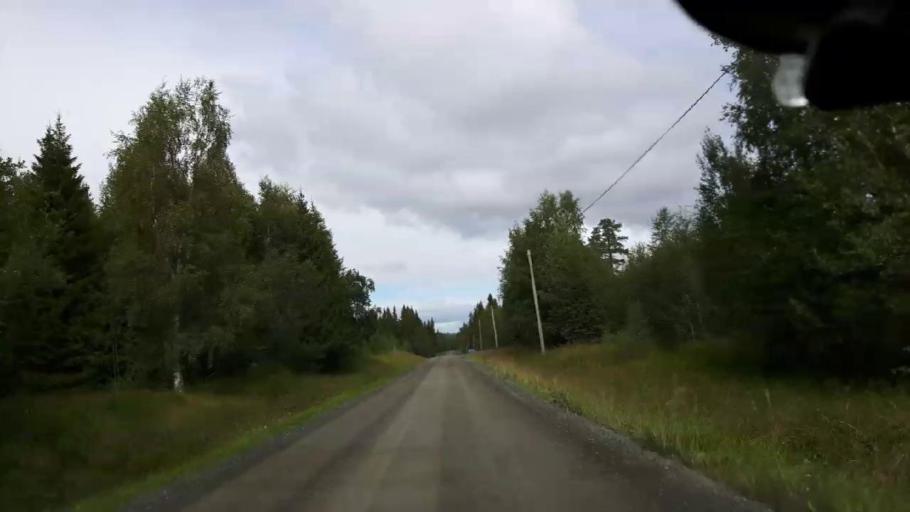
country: SE
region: Jaemtland
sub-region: Krokoms Kommun
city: Valla
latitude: 63.3932
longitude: 14.1036
